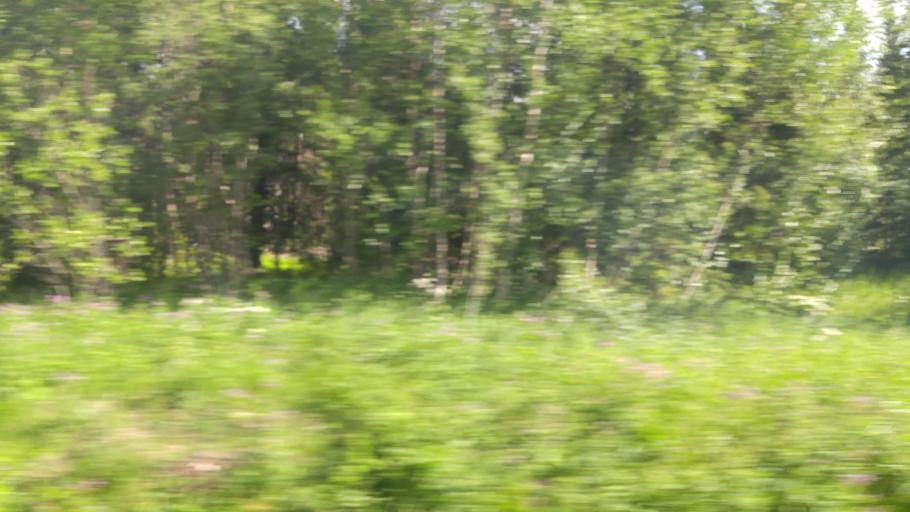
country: NO
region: Nord-Trondelag
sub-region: Meraker
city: Meraker
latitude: 63.2908
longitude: 12.3307
